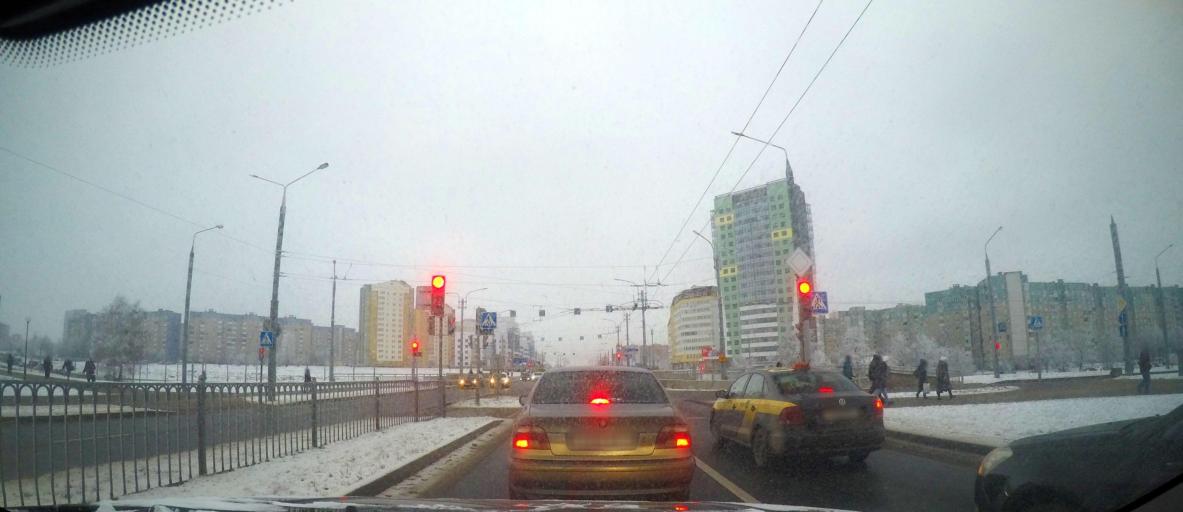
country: BY
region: Grodnenskaya
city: Hrodna
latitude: 53.6520
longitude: 23.8547
